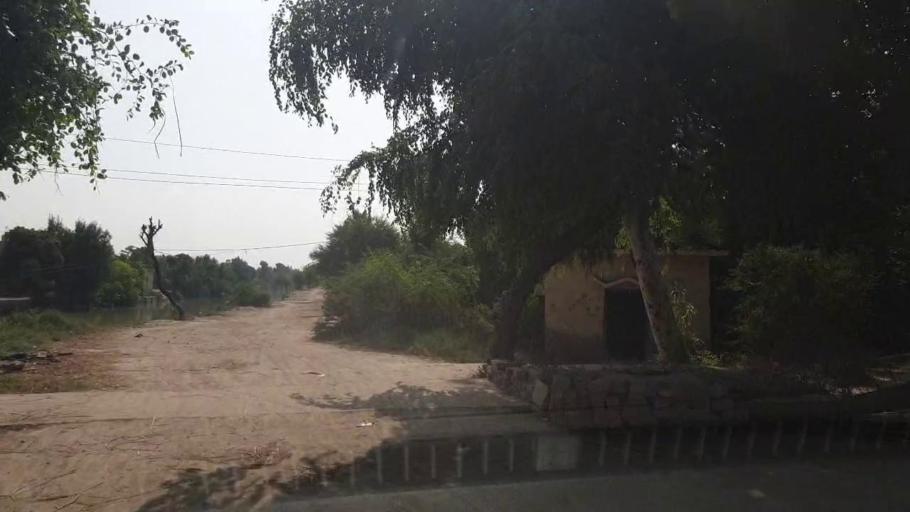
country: PK
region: Sindh
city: Badin
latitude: 24.6515
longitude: 68.8444
